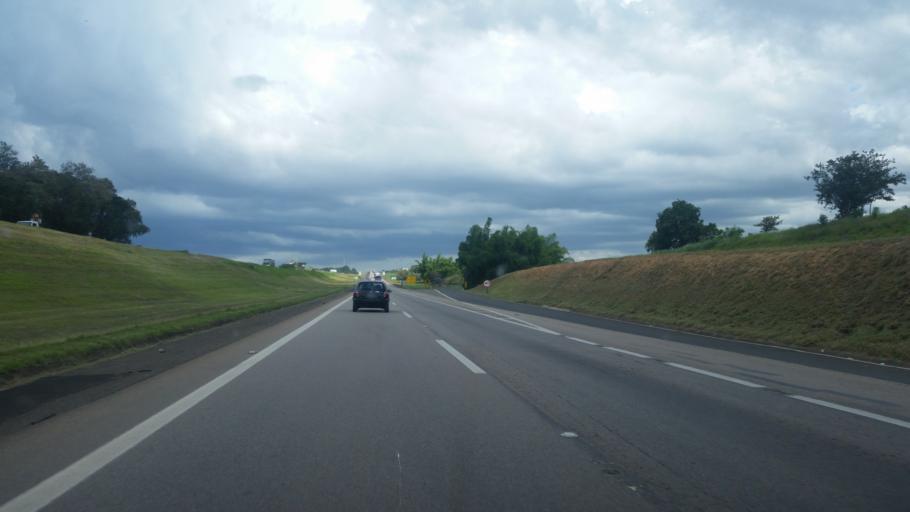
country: BR
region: Sao Paulo
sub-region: Boituva
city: Boituva
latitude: -23.2893
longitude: -47.7515
